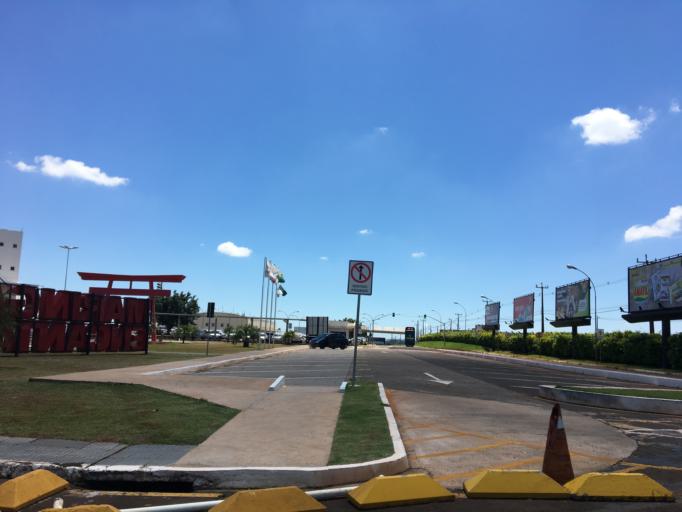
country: BR
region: Parana
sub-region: Paicandu
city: Paicandu
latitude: -23.4802
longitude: -52.0124
